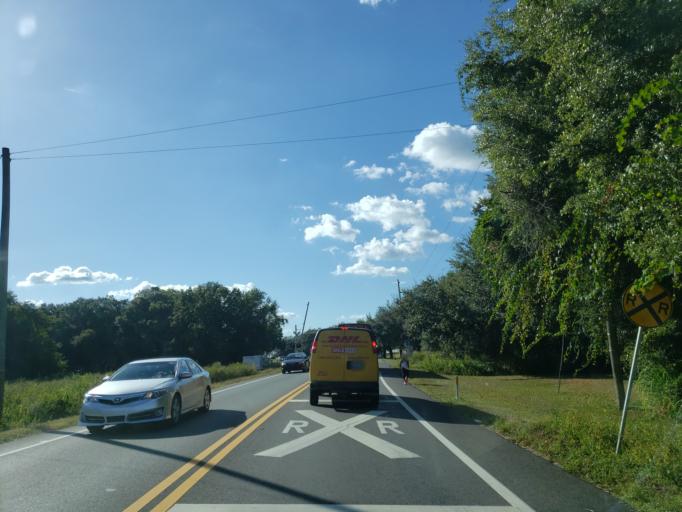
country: US
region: Florida
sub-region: Hillsborough County
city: Plant City
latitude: 28.0040
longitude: -82.1425
